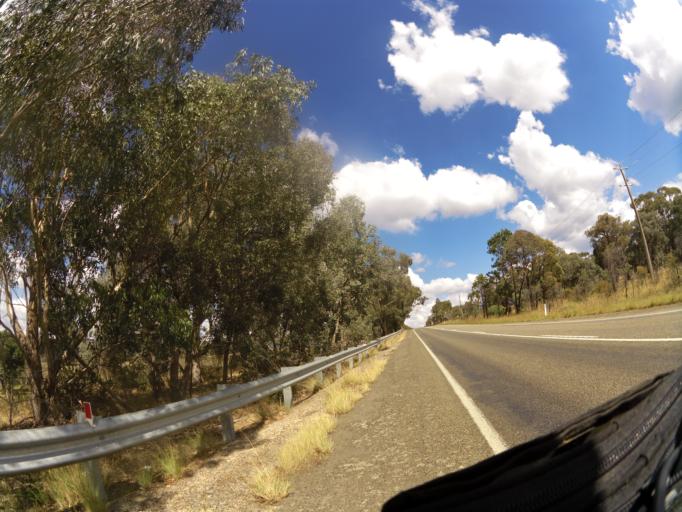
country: AU
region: Victoria
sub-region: Benalla
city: Benalla
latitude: -36.7899
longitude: 146.0108
